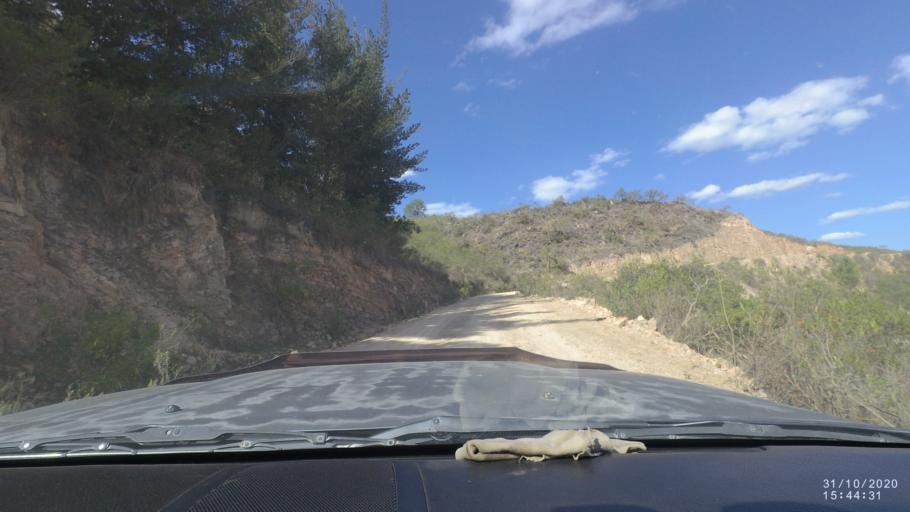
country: BO
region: Chuquisaca
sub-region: Provincia Zudanez
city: Mojocoya
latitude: -18.3177
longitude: -64.7230
